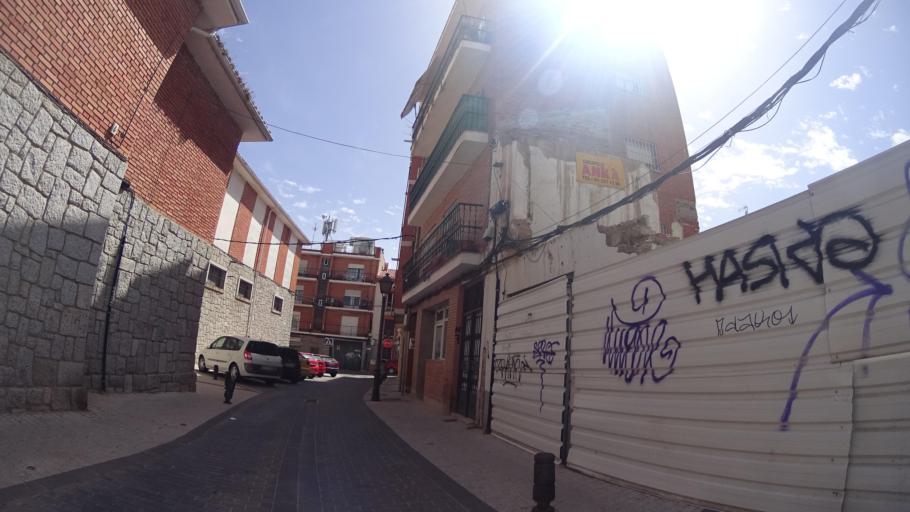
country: ES
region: Madrid
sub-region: Provincia de Madrid
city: Colmenar Viejo
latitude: 40.6585
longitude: -3.7684
